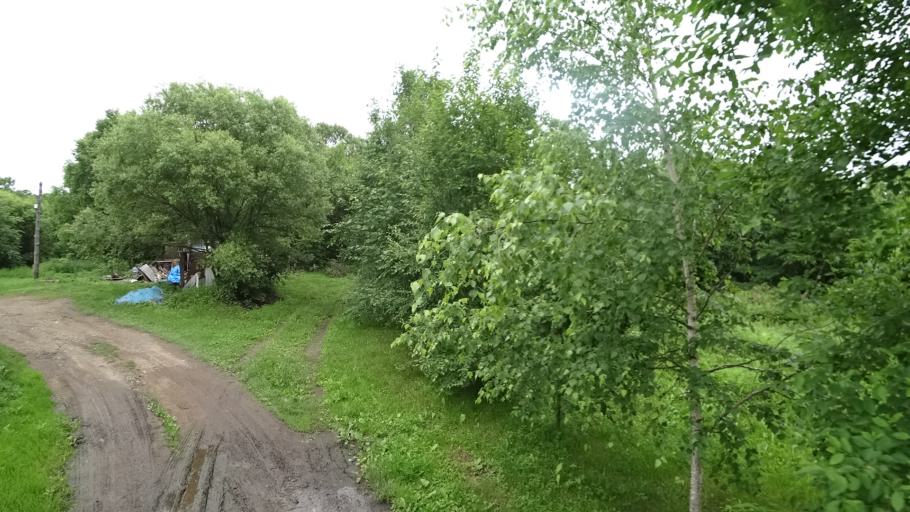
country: RU
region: Primorskiy
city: Novosysoyevka
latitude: 44.2081
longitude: 133.3387
